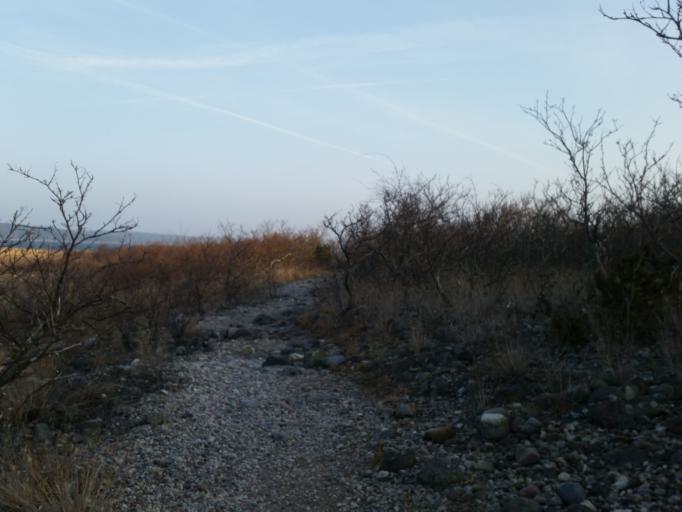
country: SE
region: Kalmar
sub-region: Vasterviks Kommun
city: Vaestervik
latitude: 57.3664
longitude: 17.0991
